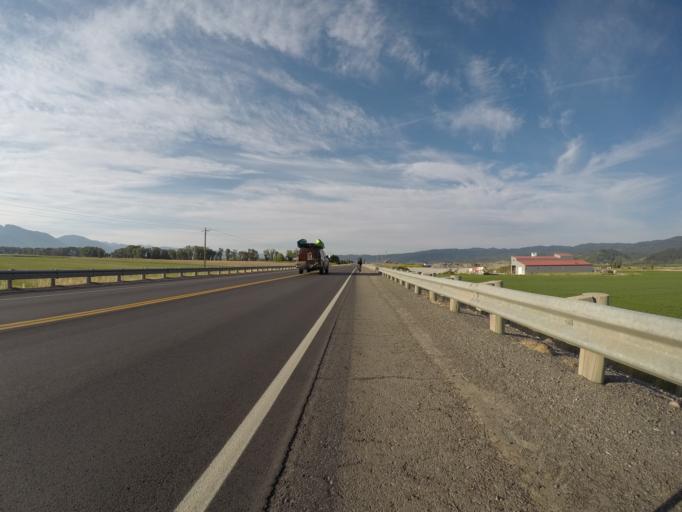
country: US
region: Wyoming
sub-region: Lincoln County
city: Afton
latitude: 42.9735
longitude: -111.0124
